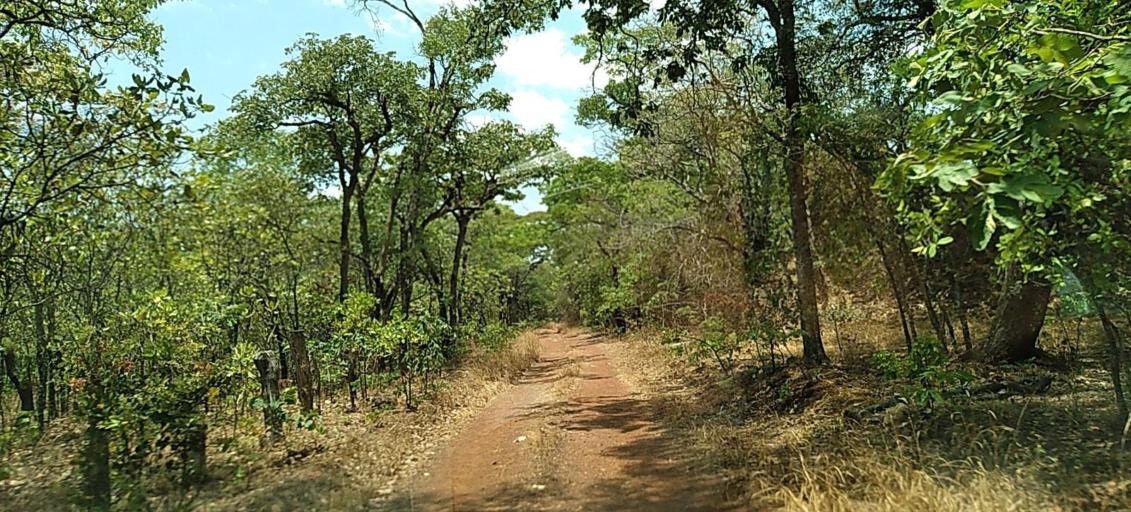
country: ZM
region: Copperbelt
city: Chililabombwe
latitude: -12.4499
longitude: 27.6968
